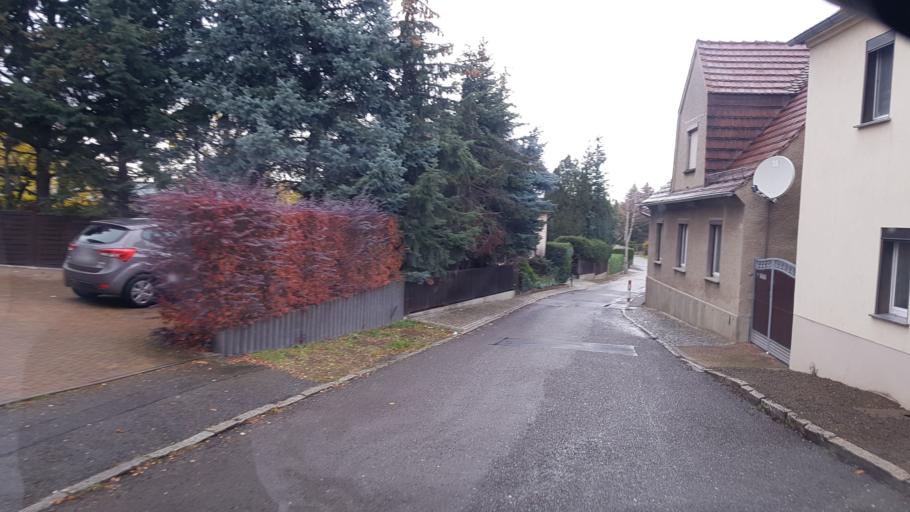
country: DE
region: Brandenburg
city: Ortrand
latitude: 51.3747
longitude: 13.7635
